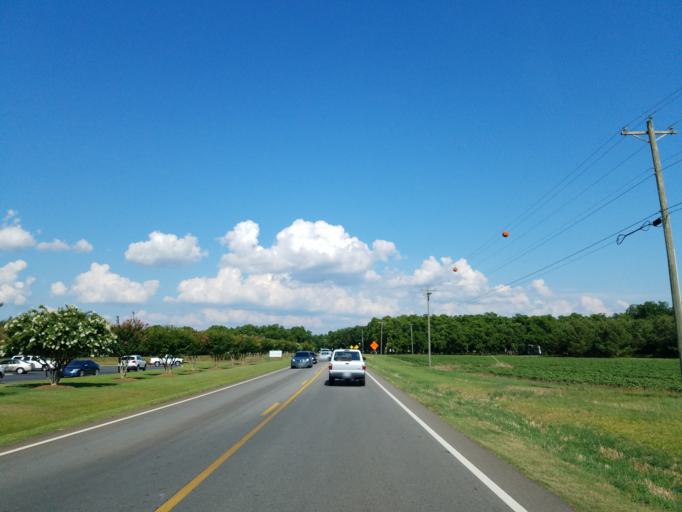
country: US
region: Georgia
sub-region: Peach County
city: Fort Valley
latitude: 32.5548
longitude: -83.8273
